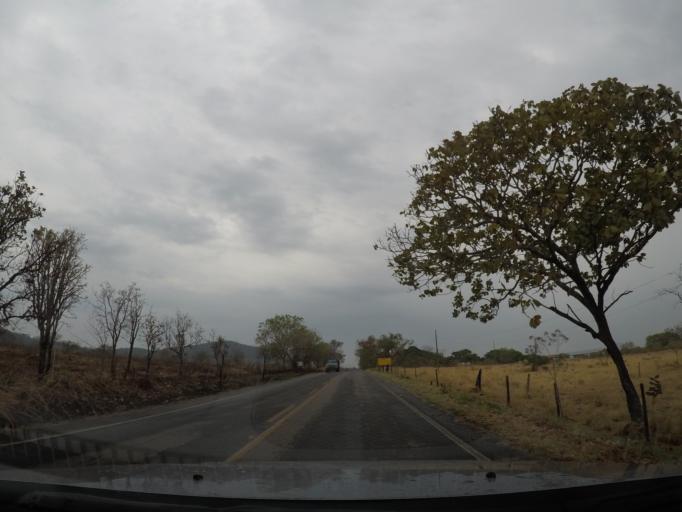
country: BR
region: Goias
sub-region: Pirenopolis
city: Pirenopolis
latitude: -15.8510
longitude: -48.9324
